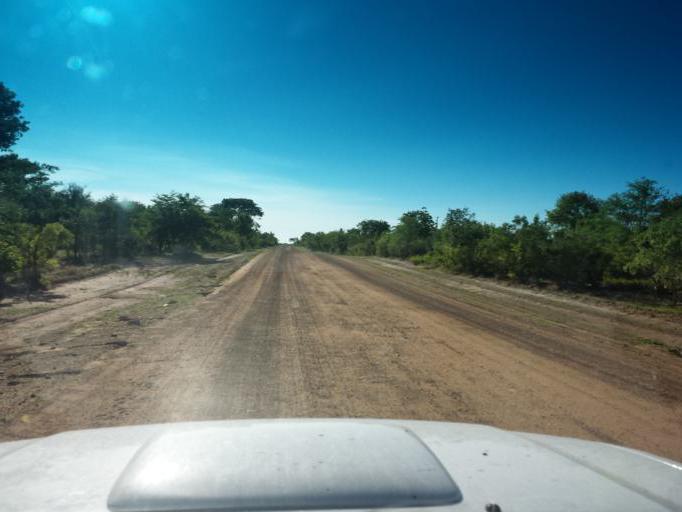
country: BW
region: North West
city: Shakawe
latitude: -18.2412
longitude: 21.7417
